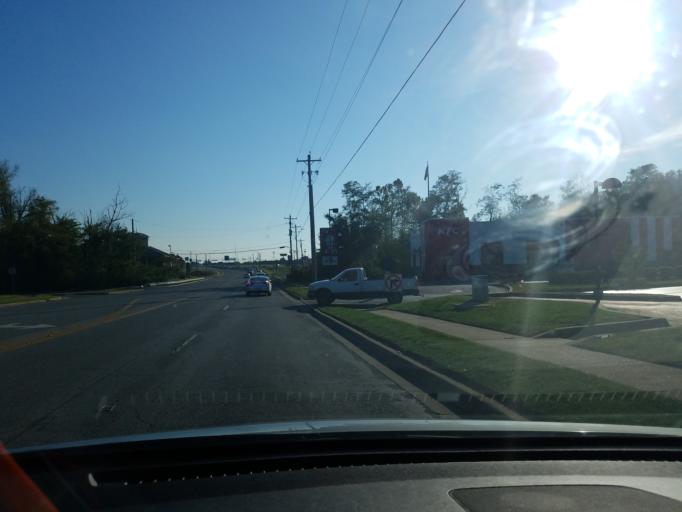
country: US
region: Indiana
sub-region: Clark County
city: Sellersburg
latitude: 38.3495
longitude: -85.7962
